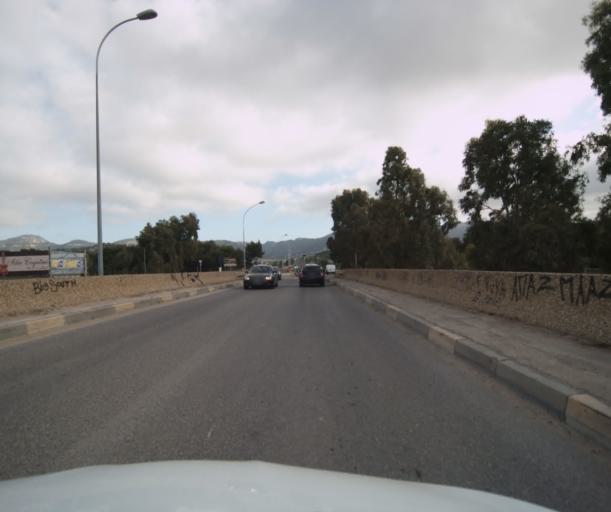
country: FR
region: Provence-Alpes-Cote d'Azur
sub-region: Departement du Var
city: Ollioules
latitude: 43.1192
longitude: 5.8473
